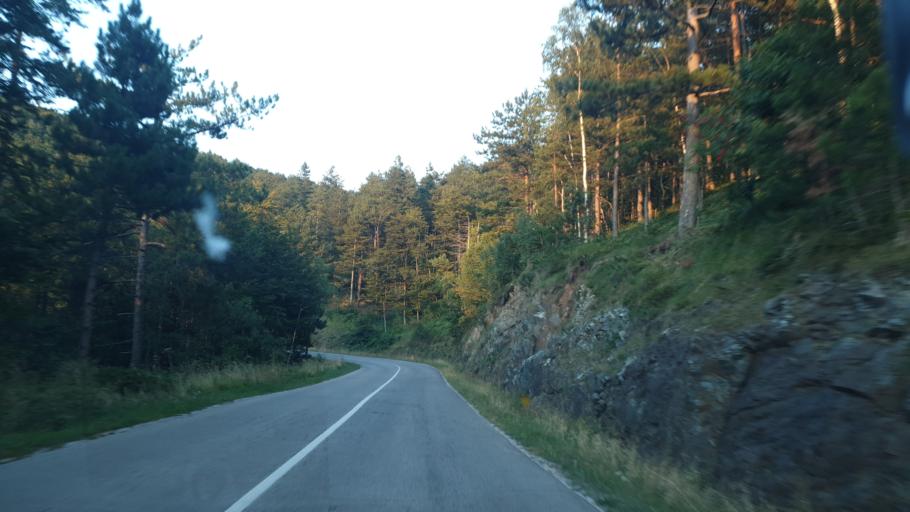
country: RS
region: Central Serbia
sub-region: Zlatiborski Okrug
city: Kosjeric
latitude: 44.0928
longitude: 19.9913
